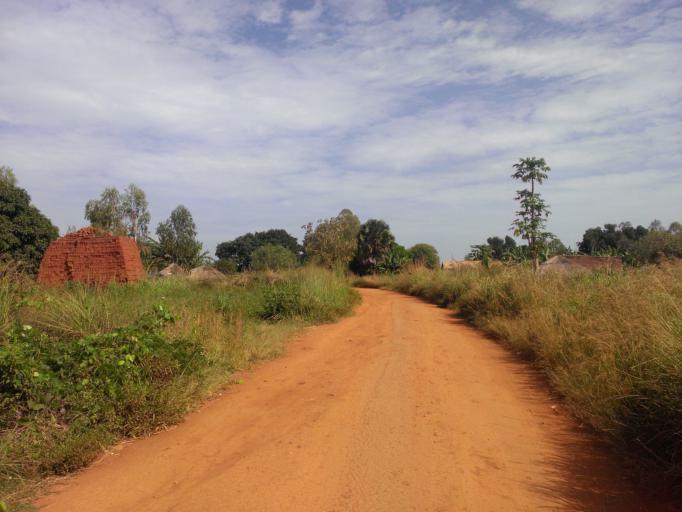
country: UG
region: Northern Region
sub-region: Gulu District
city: Gulu
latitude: 2.7862
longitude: 32.3181
